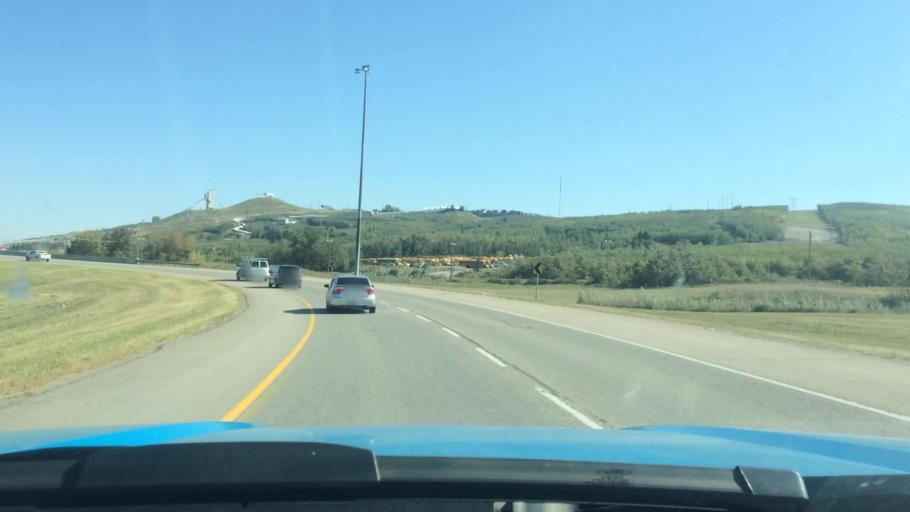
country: CA
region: Alberta
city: Calgary
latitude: 51.0867
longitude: -114.2329
